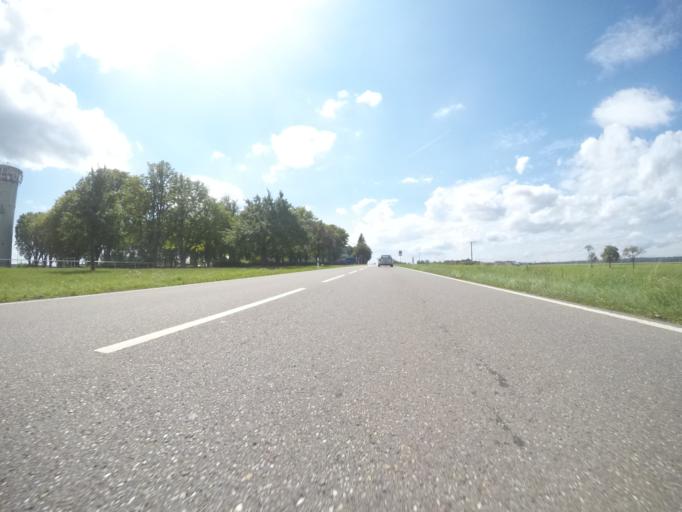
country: DE
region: Baden-Wuerttemberg
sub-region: Karlsruhe Region
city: Pfalzgrafenweiler
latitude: 48.5326
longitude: 8.5616
